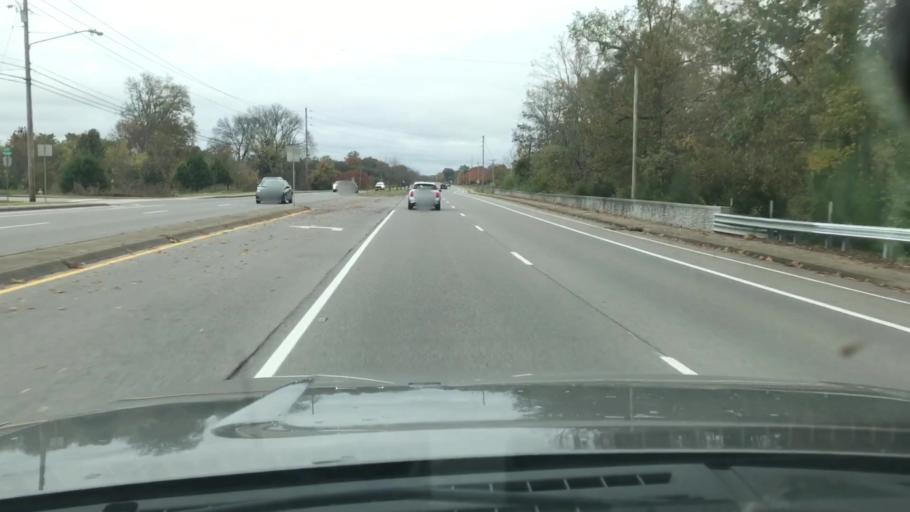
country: US
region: Tennessee
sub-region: Williamson County
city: Franklin
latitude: 35.9559
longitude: -86.8837
